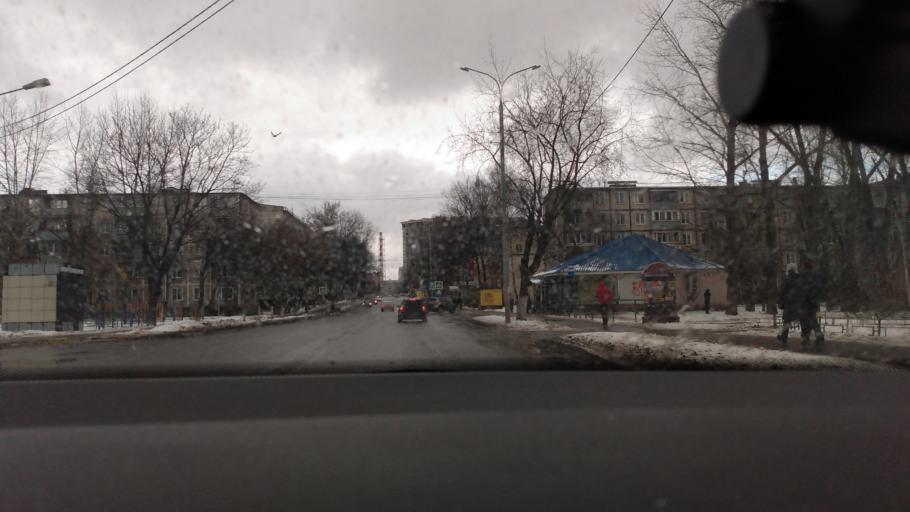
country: RU
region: Moskovskaya
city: Shchelkovo
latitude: 55.9166
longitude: 37.9908
